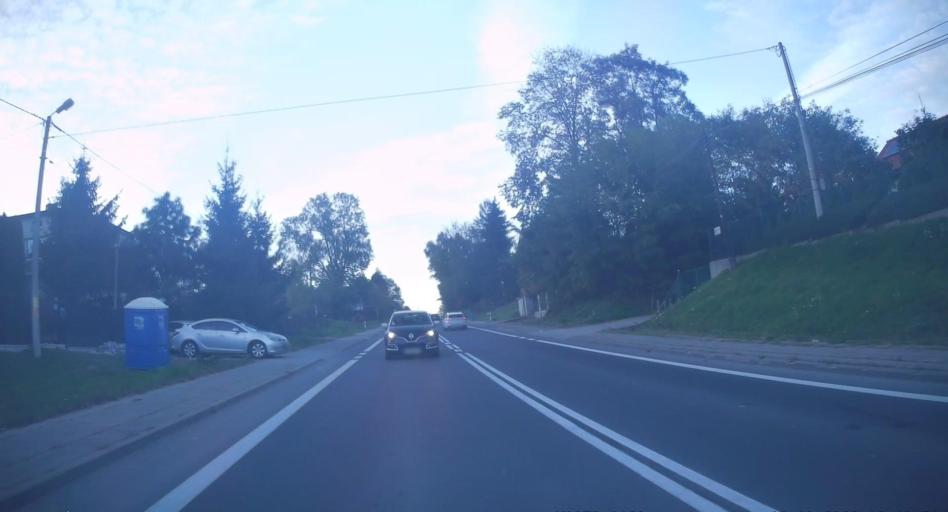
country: PL
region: Lesser Poland Voivodeship
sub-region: Powiat krakowski
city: Wielka Wies
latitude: 50.1471
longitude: 19.8573
